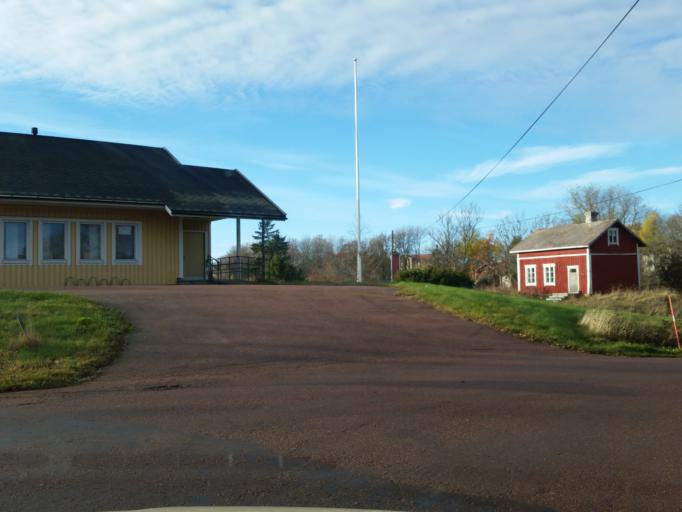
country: AX
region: Alands skaergard
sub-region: Kumlinge
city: Kumlinge
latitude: 60.2602
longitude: 20.7789
